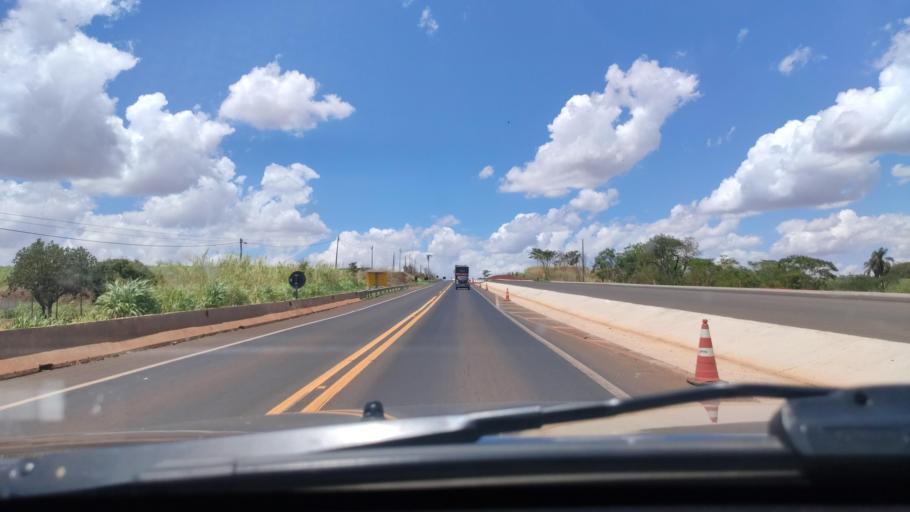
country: BR
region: Sao Paulo
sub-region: Jau
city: Jau
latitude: -22.2360
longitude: -48.5360
